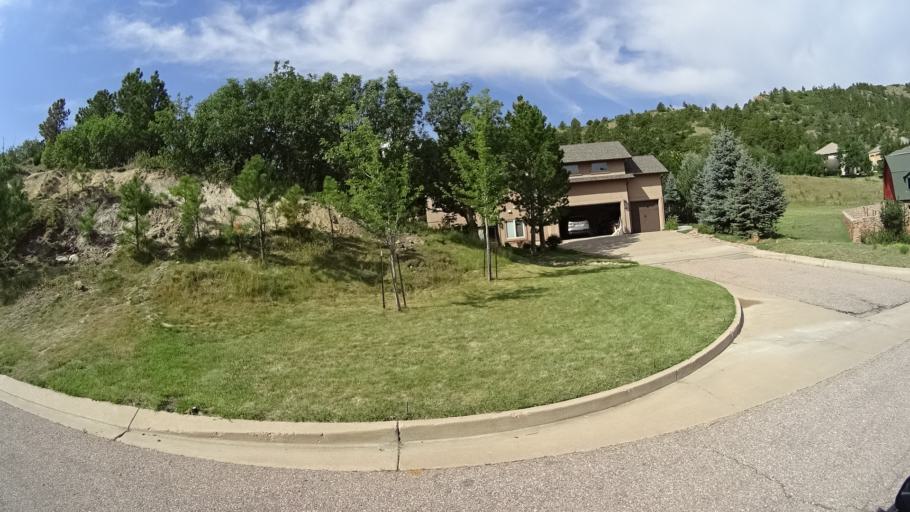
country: US
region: Colorado
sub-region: El Paso County
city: Air Force Academy
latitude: 38.9429
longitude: -104.8695
